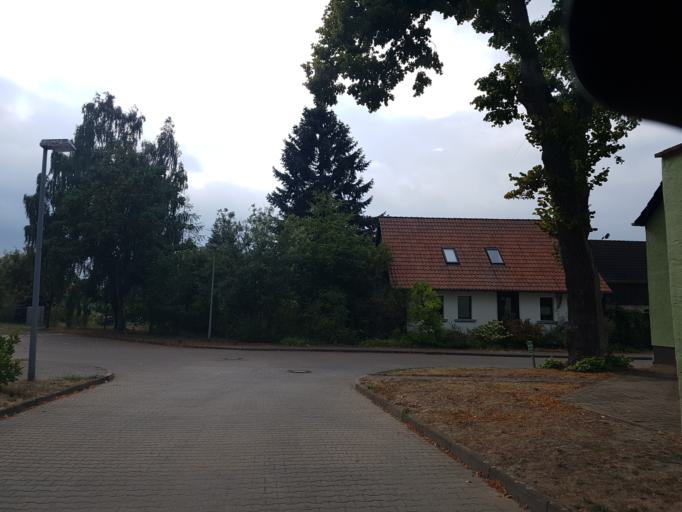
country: DE
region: Saxony-Anhalt
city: Rosslau
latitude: 52.0334
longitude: 12.2845
